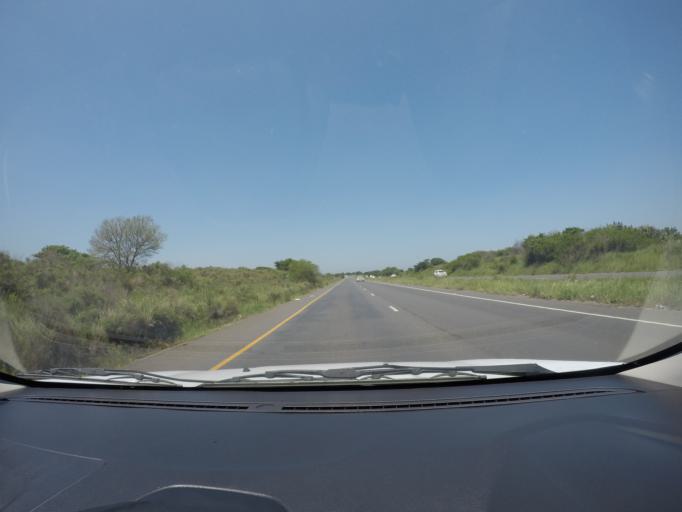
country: ZA
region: KwaZulu-Natal
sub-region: uThungulu District Municipality
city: Richards Bay
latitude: -28.7801
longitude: 31.9937
